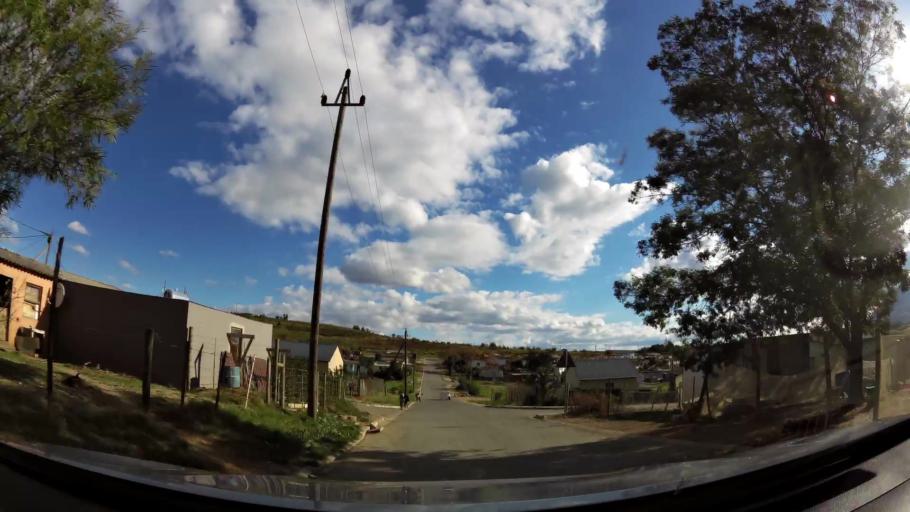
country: ZA
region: Western Cape
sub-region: Overberg District Municipality
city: Swellendam
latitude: -34.0356
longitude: 20.4511
